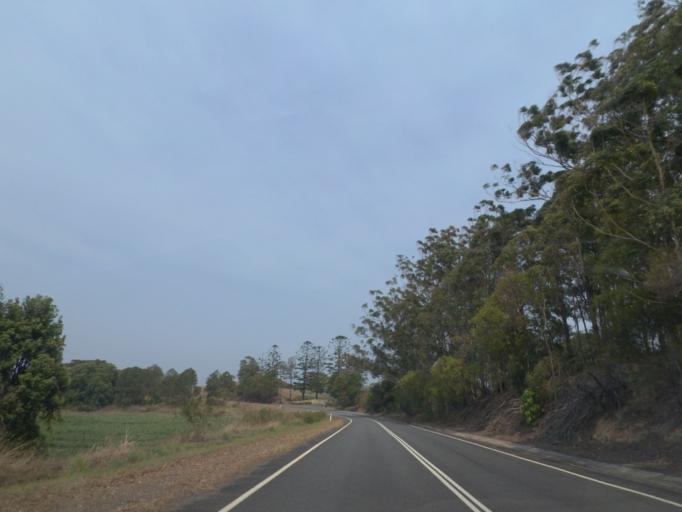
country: AU
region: New South Wales
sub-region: Tweed
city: Burringbar
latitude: -28.4582
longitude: 153.5225
